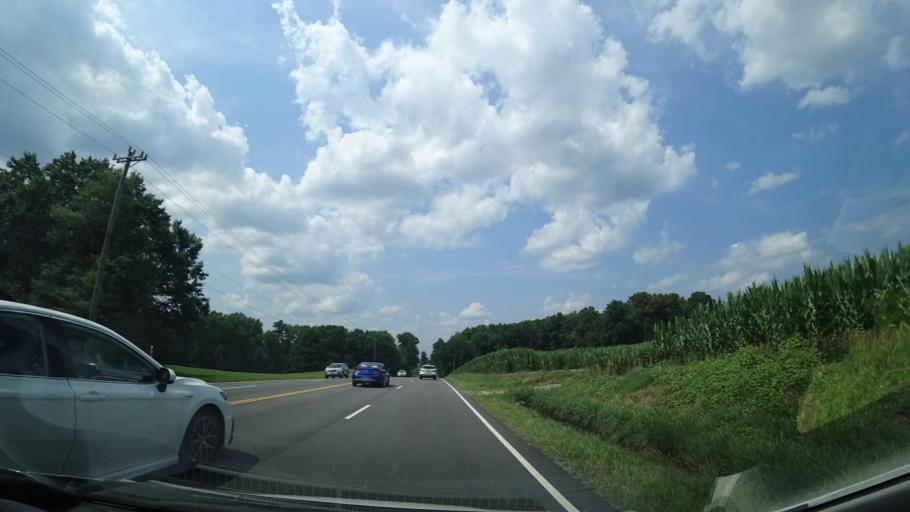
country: US
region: Virginia
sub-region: Hanover County
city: Ashland
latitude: 37.8697
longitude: -77.4642
